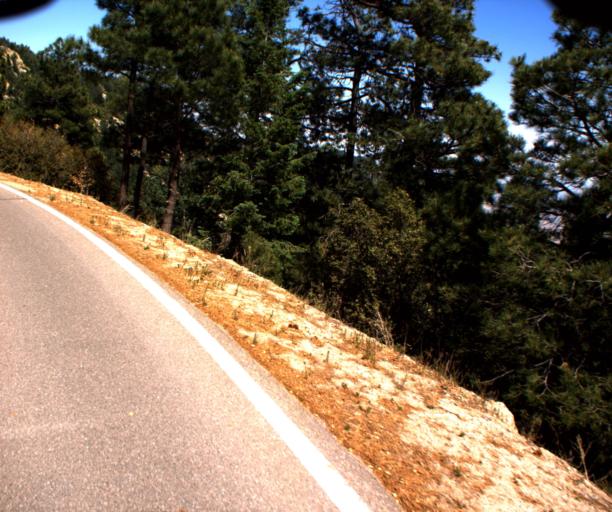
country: US
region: Arizona
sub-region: Graham County
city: Swift Trail Junction
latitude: 32.6204
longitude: -109.8259
